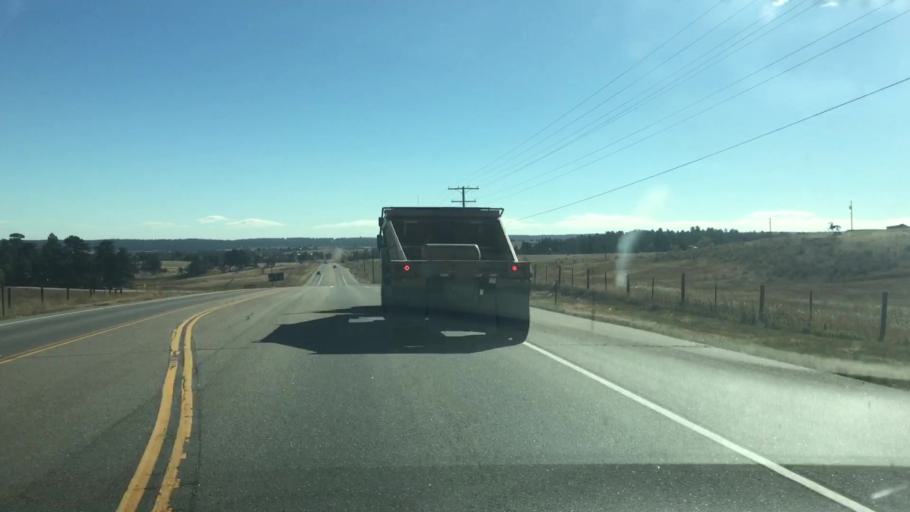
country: US
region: Colorado
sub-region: Elbert County
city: Ponderosa Park
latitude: 39.3620
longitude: -104.6571
